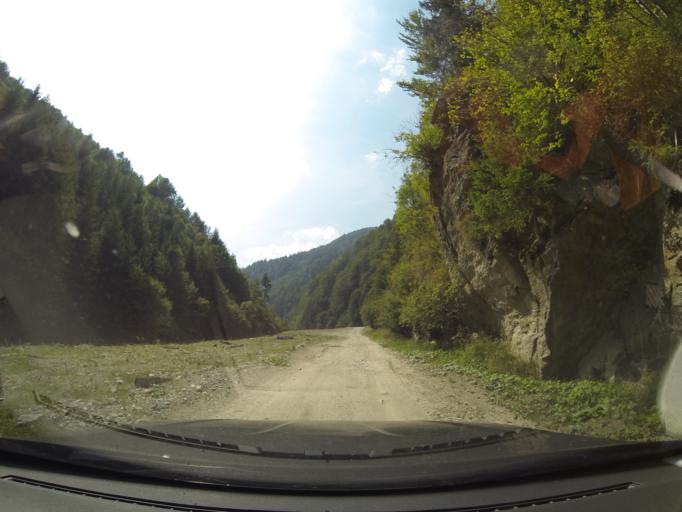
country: RO
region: Arges
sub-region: Comuna Arefu
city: Arefu
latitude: 45.4934
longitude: 24.6426
